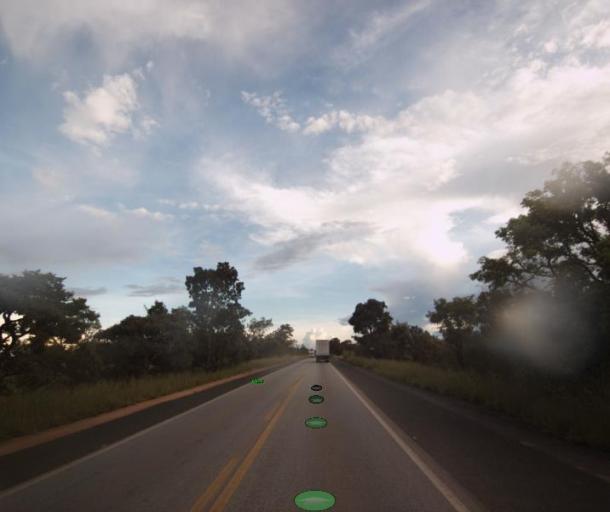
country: BR
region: Goias
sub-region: Uruacu
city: Uruacu
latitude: -14.0501
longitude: -49.0895
